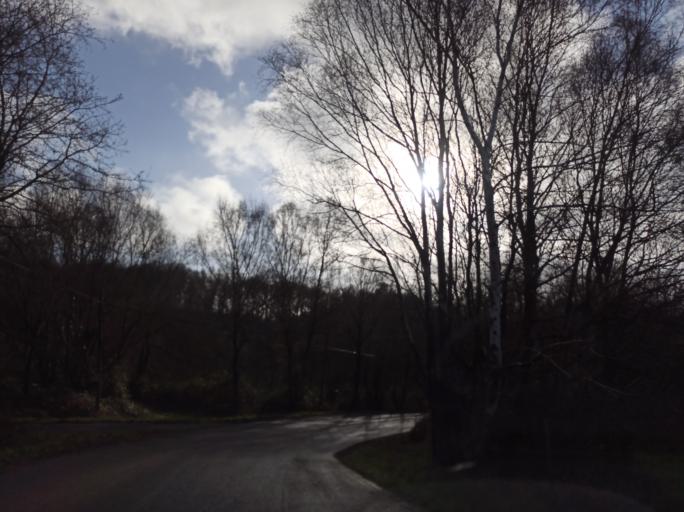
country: ES
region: Galicia
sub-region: Provincia da Coruna
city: Sobrado
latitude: 43.0920
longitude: -7.9704
